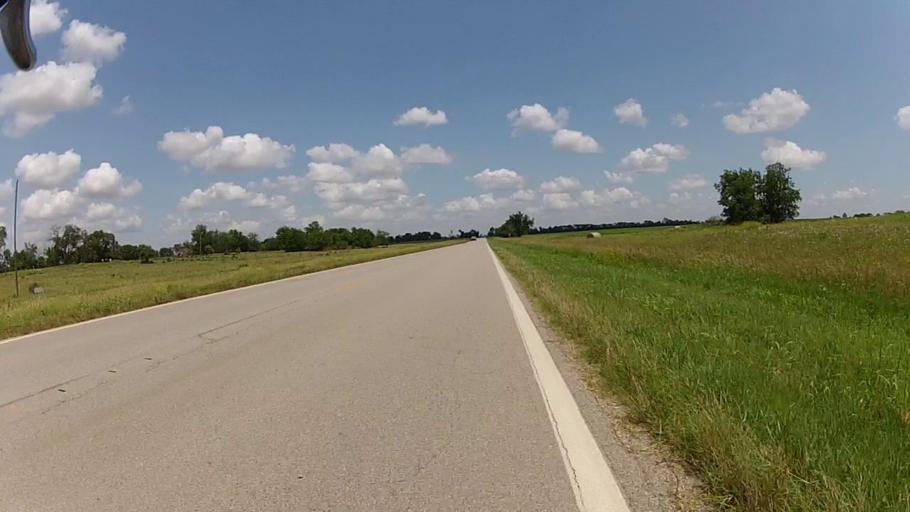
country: US
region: Kansas
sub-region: Labette County
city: Altamont
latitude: 37.1926
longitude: -95.3760
